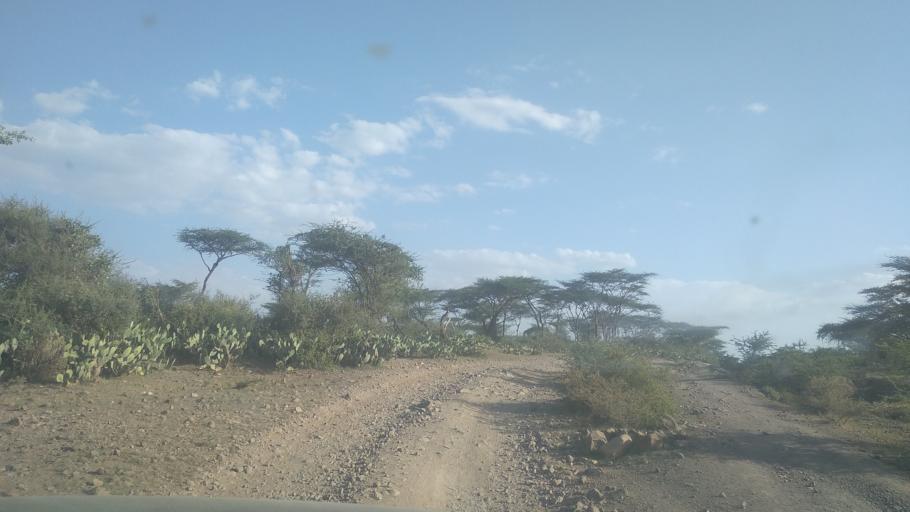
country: ET
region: Oromiya
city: Hirna
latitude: 9.4200
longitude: 40.9618
